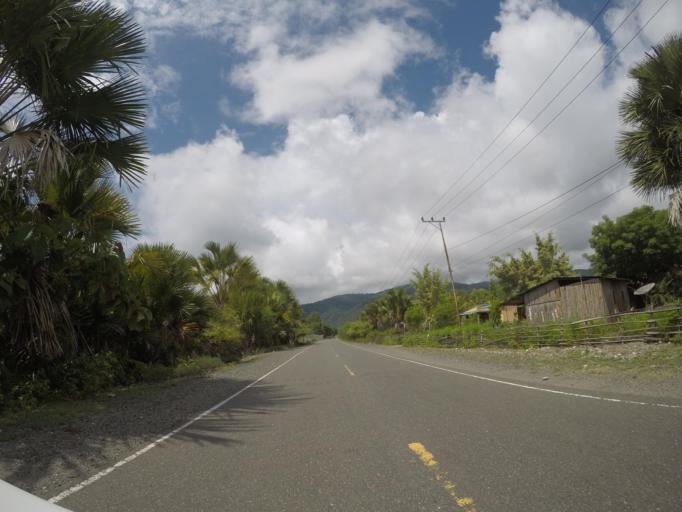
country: TL
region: Liquica
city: Maubara
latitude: -8.7203
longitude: 125.1099
